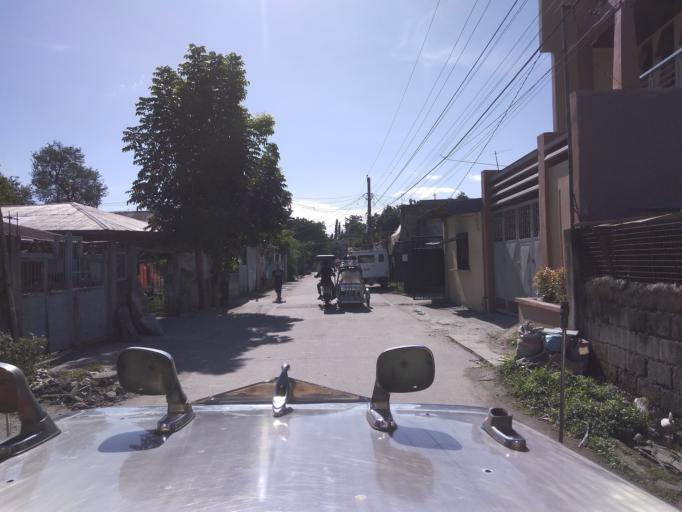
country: PH
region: Central Luzon
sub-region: Province of Pampanga
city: Calibutbut
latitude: 15.1005
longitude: 120.6050
